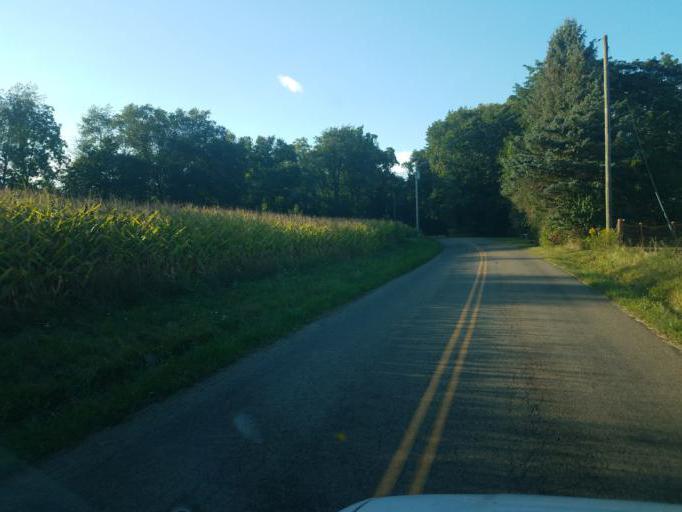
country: US
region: Ohio
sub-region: Knox County
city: Fredericktown
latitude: 40.4132
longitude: -82.5976
